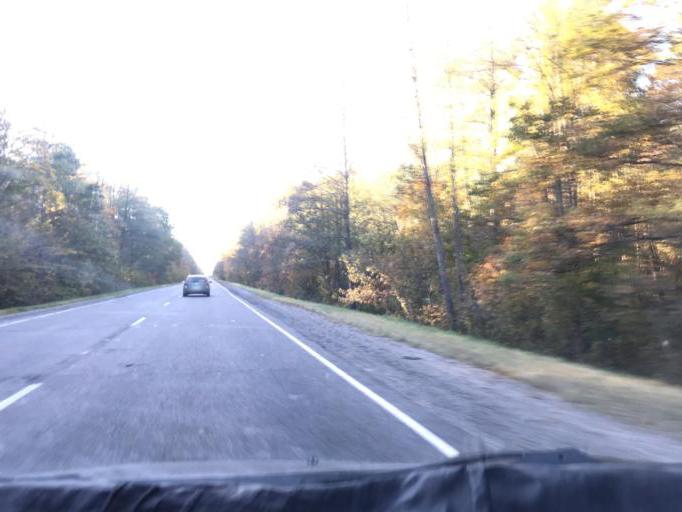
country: BY
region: Gomel
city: Pyetrykaw
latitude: 52.2657
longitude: 28.3024
